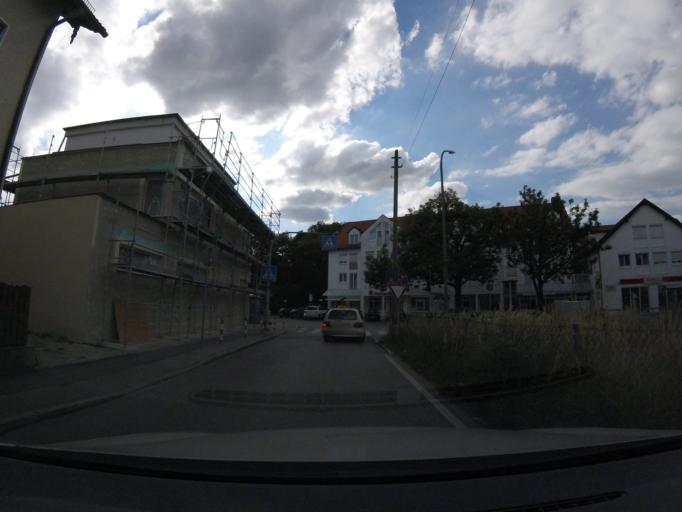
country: DE
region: Bavaria
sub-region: Upper Bavaria
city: Bogenhausen
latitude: 48.1715
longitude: 11.6266
